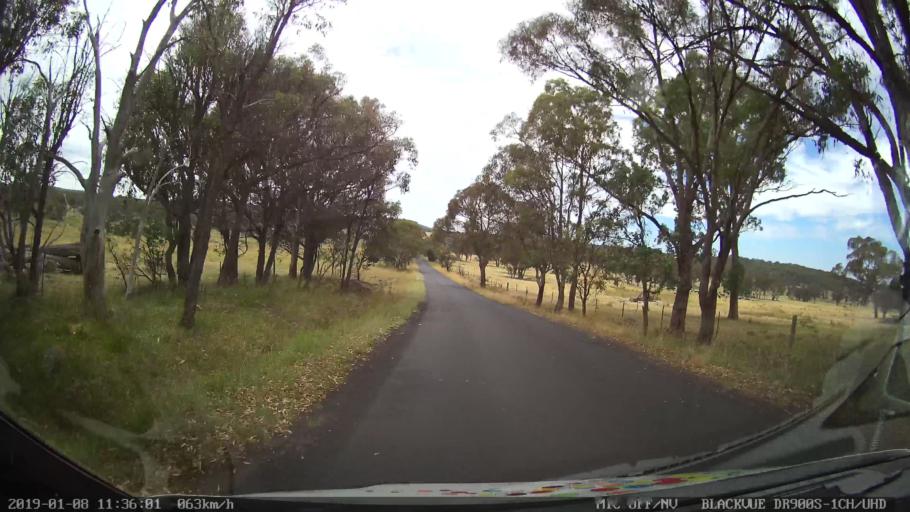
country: AU
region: New South Wales
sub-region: Guyra
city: Guyra
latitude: -30.3425
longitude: 151.5400
